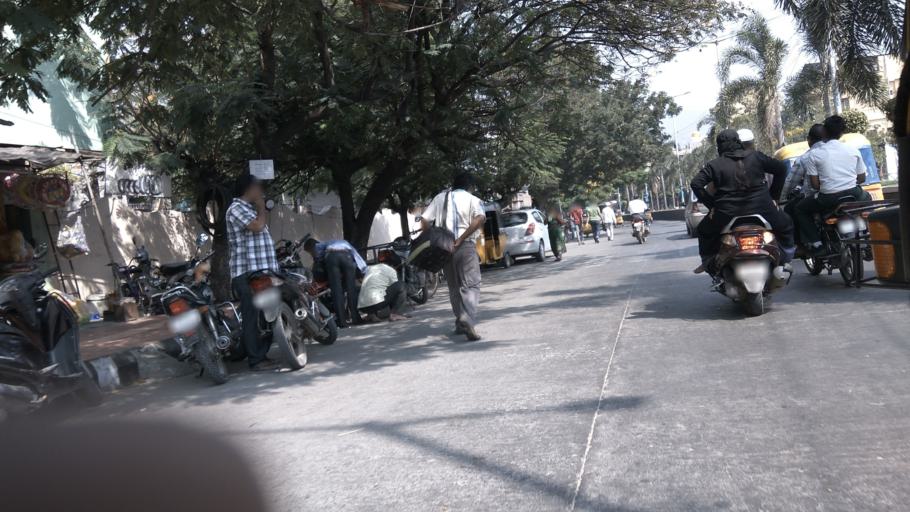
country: IN
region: Andhra Pradesh
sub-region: Chittoor
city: Tirupati
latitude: 13.6340
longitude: 79.4132
